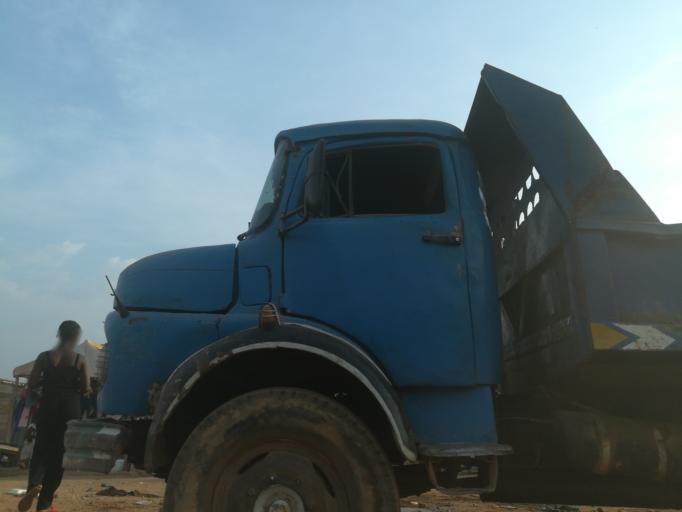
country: NG
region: Abuja Federal Capital Territory
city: Abuja
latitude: 9.1027
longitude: 7.3713
